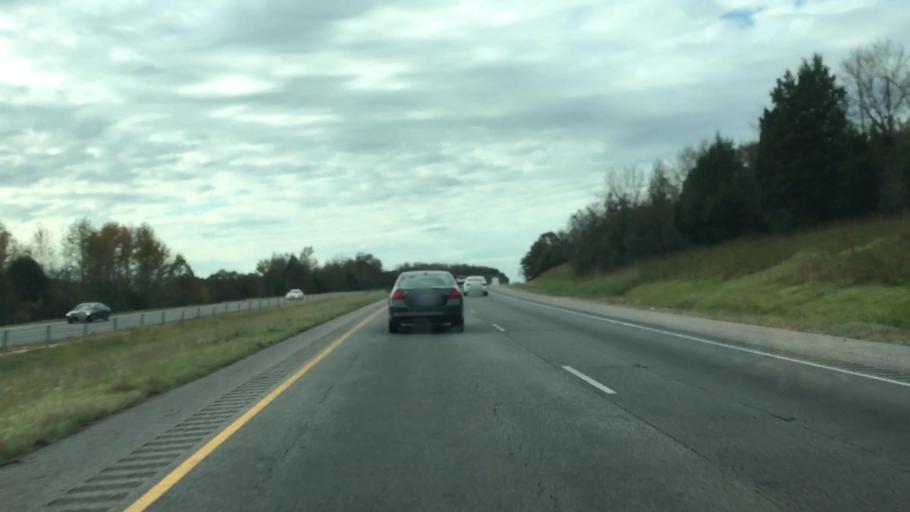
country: US
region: Arkansas
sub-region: Conway County
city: Morrilton
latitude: 35.1639
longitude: -92.6790
